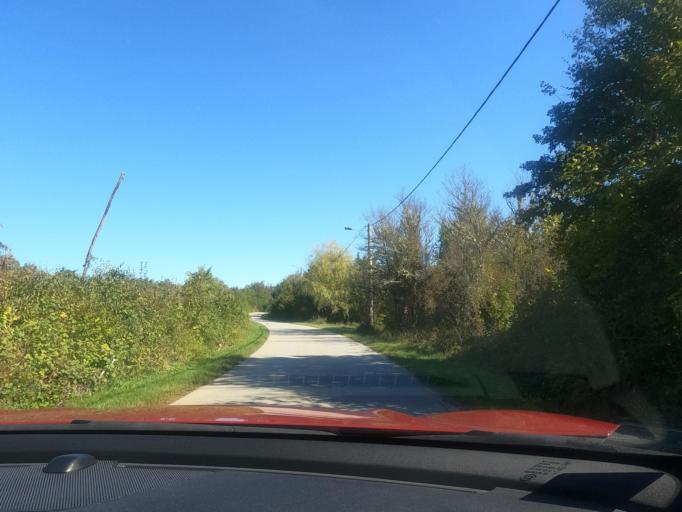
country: HR
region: Sisacko-Moslavacka
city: Petrinja
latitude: 45.3609
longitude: 16.2184
